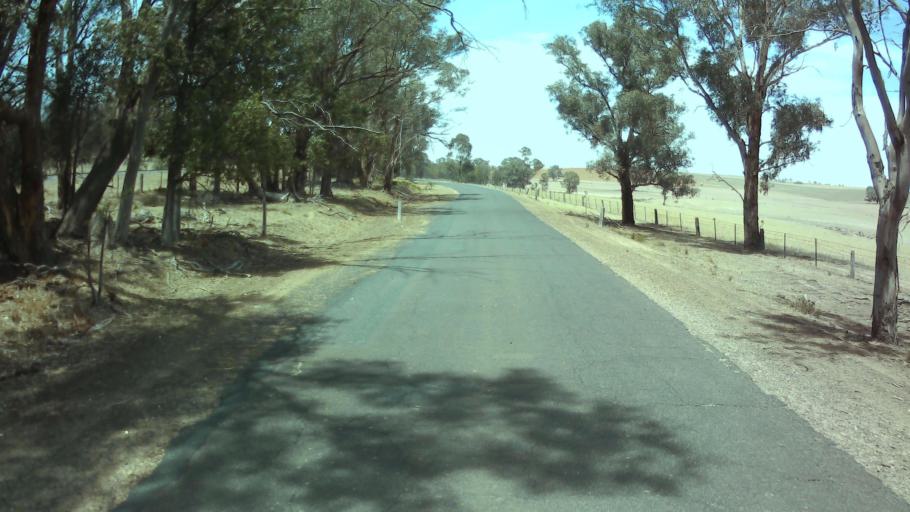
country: AU
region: New South Wales
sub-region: Weddin
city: Grenfell
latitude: -34.0219
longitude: 148.4325
